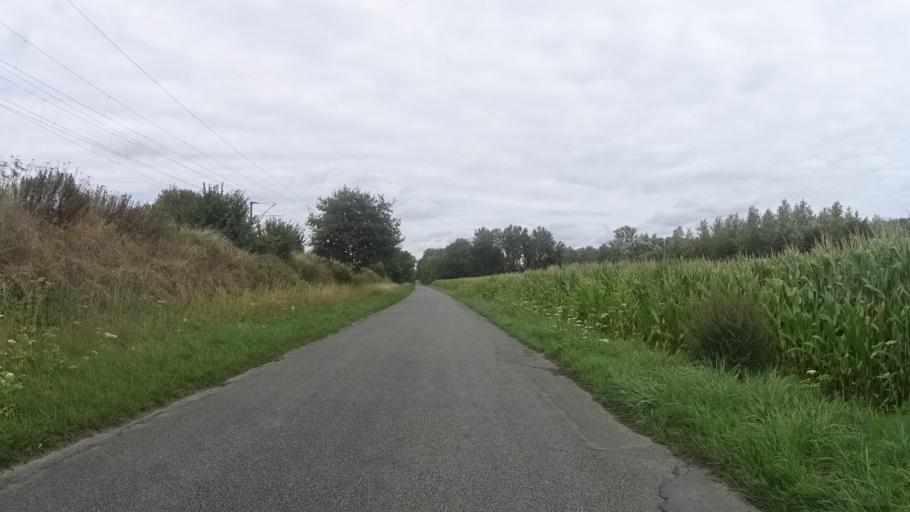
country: FR
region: Picardie
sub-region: Departement de l'Oise
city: Chiry-Ourscamp
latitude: 49.5213
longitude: 2.9507
